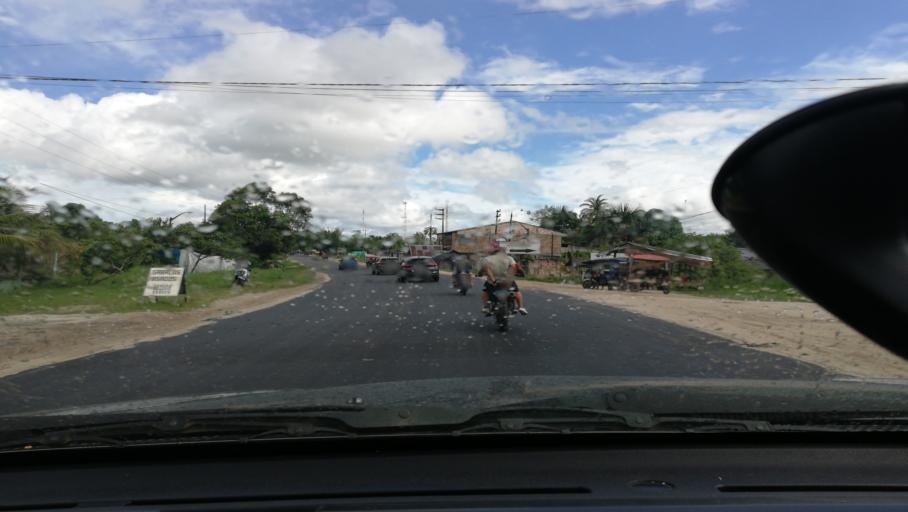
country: PE
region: Loreto
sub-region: Provincia de Maynas
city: Iquitos
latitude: -3.8209
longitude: -73.3257
